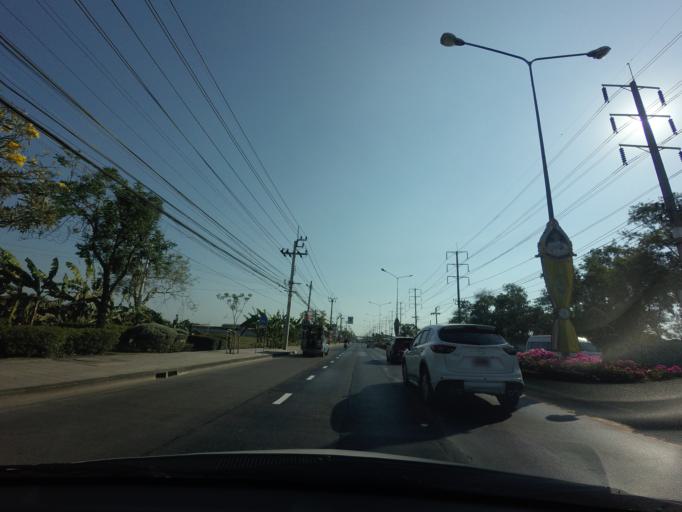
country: TH
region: Bangkok
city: Nong Chok
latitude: 13.8266
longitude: 100.8479
